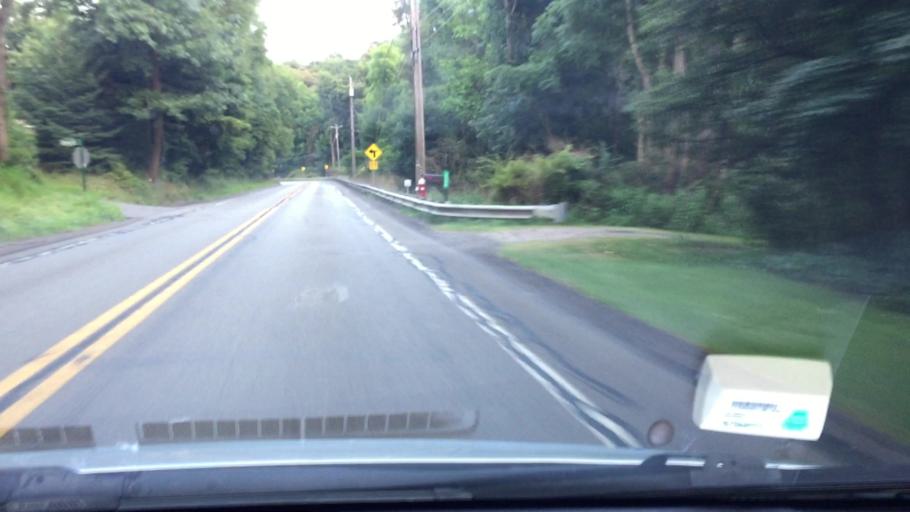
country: US
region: Pennsylvania
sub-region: Allegheny County
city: Gibsonia
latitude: 40.6321
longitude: -80.0011
